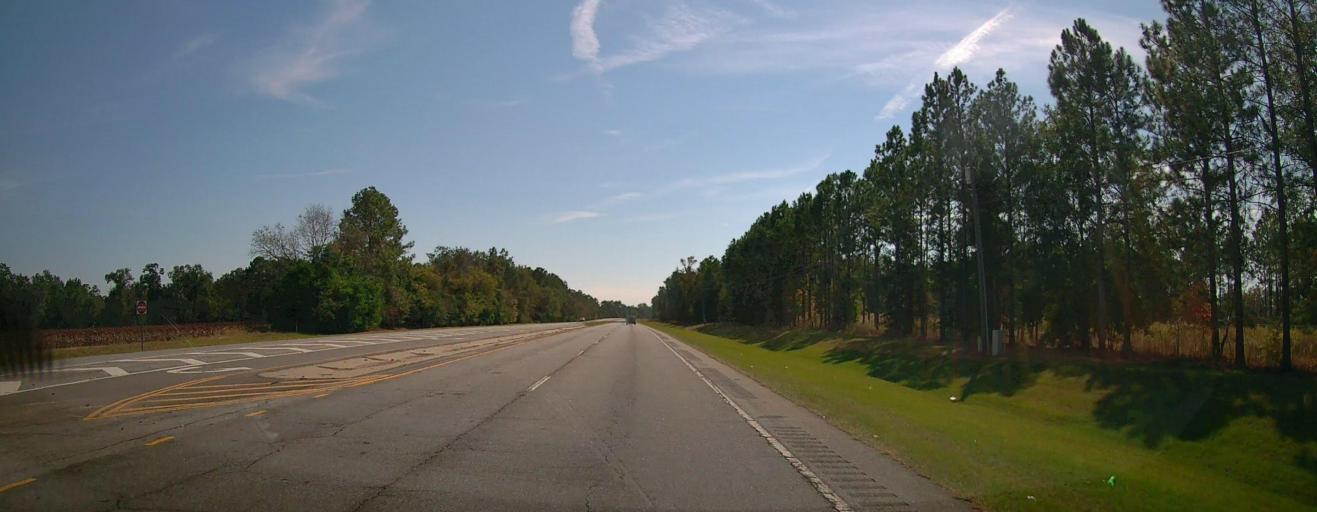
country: US
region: Georgia
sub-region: Lee County
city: Leesburg
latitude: 31.7433
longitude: -83.9871
